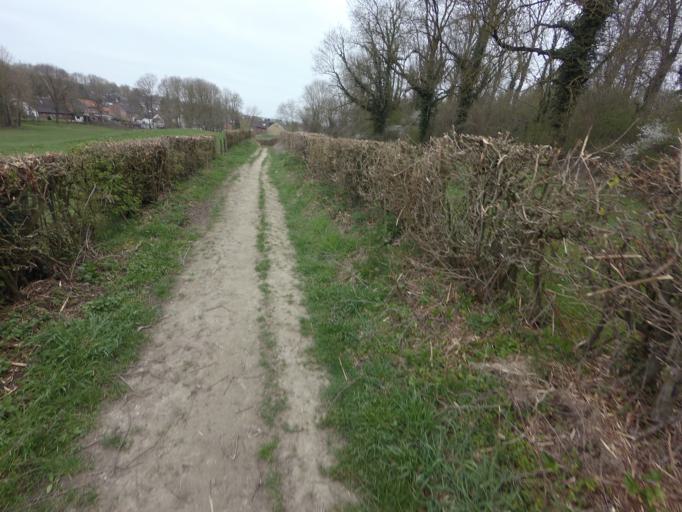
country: NL
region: Limburg
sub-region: Gemeente Voerendaal
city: Ubachsberg
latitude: 50.8260
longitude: 5.9493
